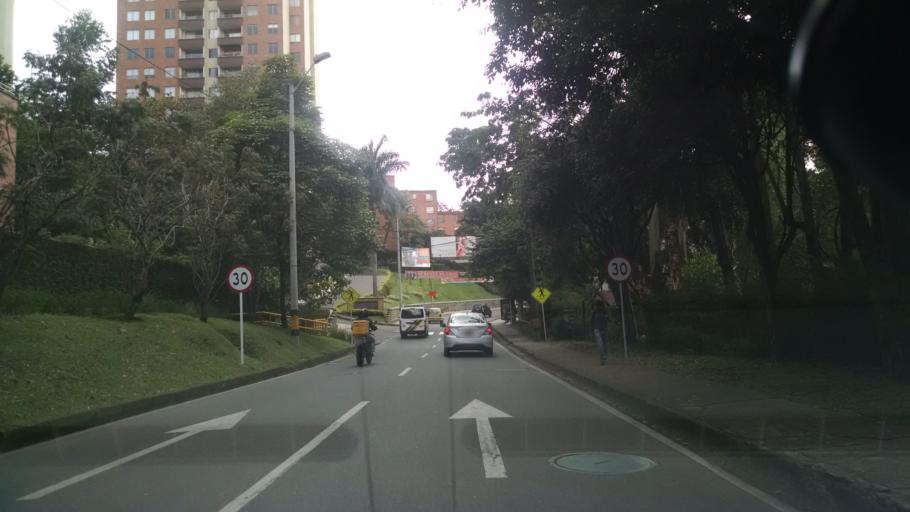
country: CO
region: Antioquia
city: Envigado
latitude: 6.2018
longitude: -75.5620
